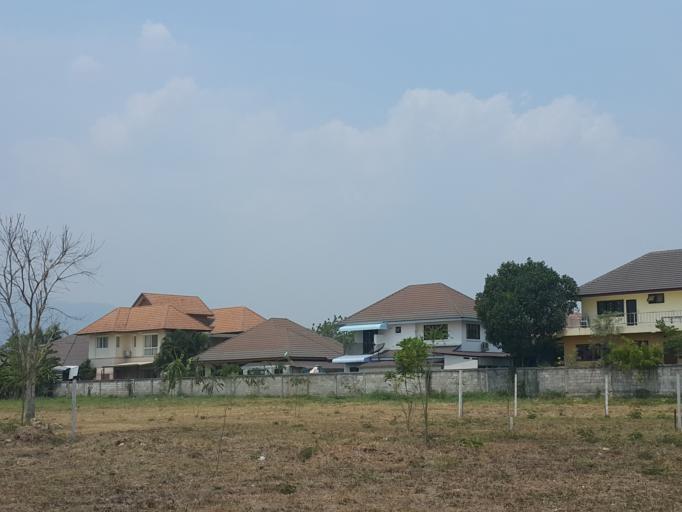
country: TH
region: Chiang Mai
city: Chiang Mai
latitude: 18.7369
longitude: 98.9670
